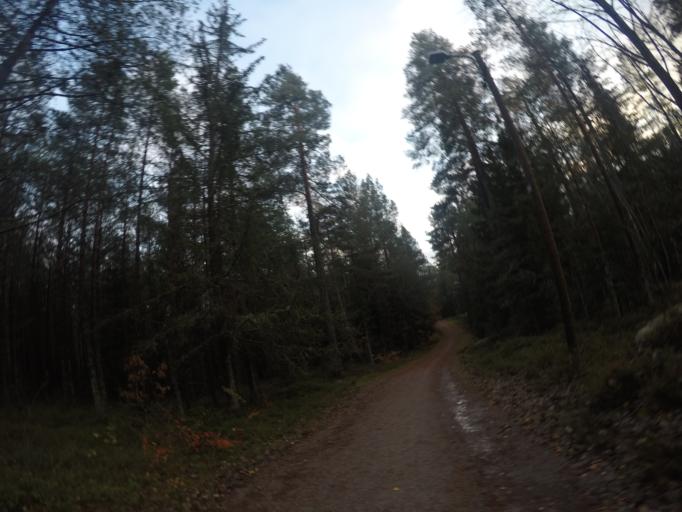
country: SE
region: Soedermanland
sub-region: Eskilstuna Kommun
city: Eskilstuna
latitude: 59.3423
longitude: 16.5238
